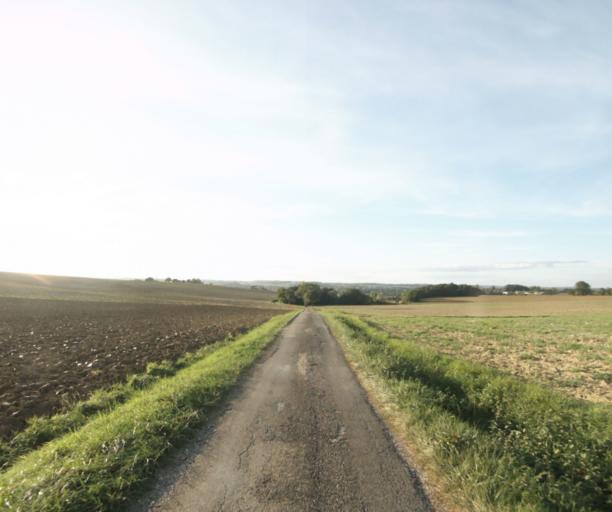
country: FR
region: Midi-Pyrenees
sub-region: Departement du Gers
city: Gondrin
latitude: 43.8756
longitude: 0.3072
